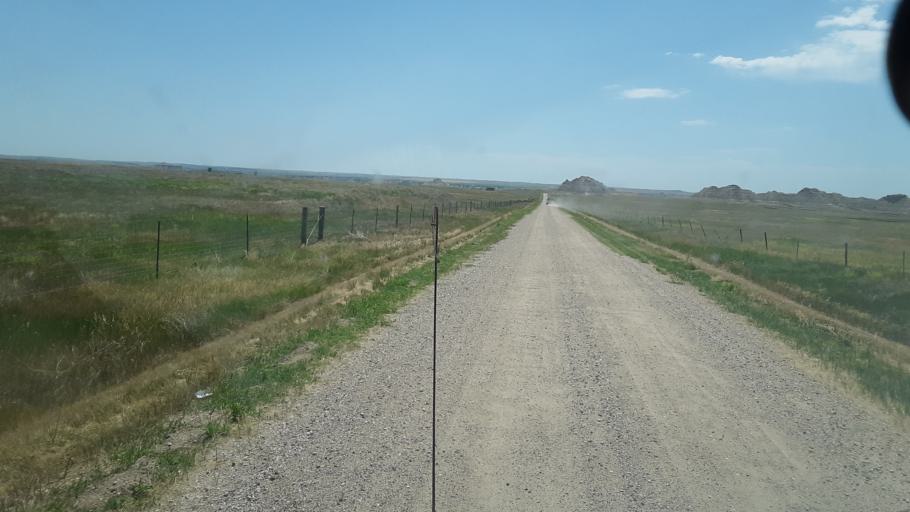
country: US
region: South Dakota
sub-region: Haakon County
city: Philip
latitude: 43.7468
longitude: -101.9995
